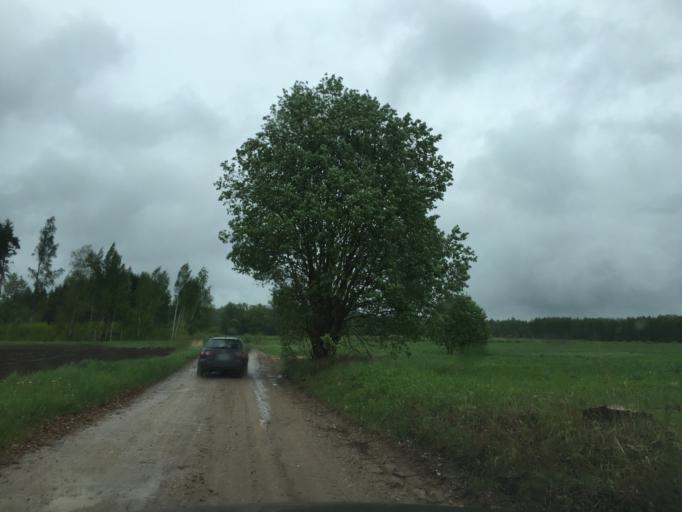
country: LV
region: Ogre
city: Jumprava
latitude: 56.6738
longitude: 25.0076
